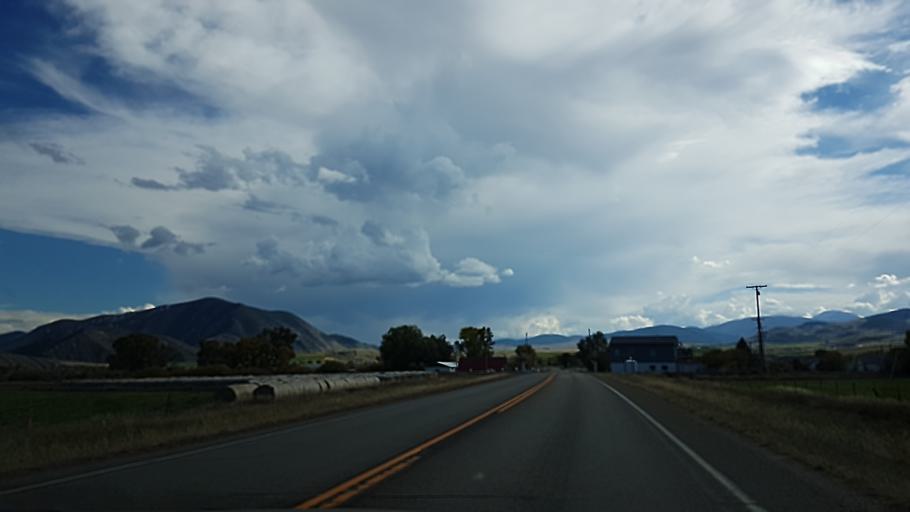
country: US
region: Montana
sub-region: Jefferson County
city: Whitehall
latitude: 45.8624
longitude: -111.9531
